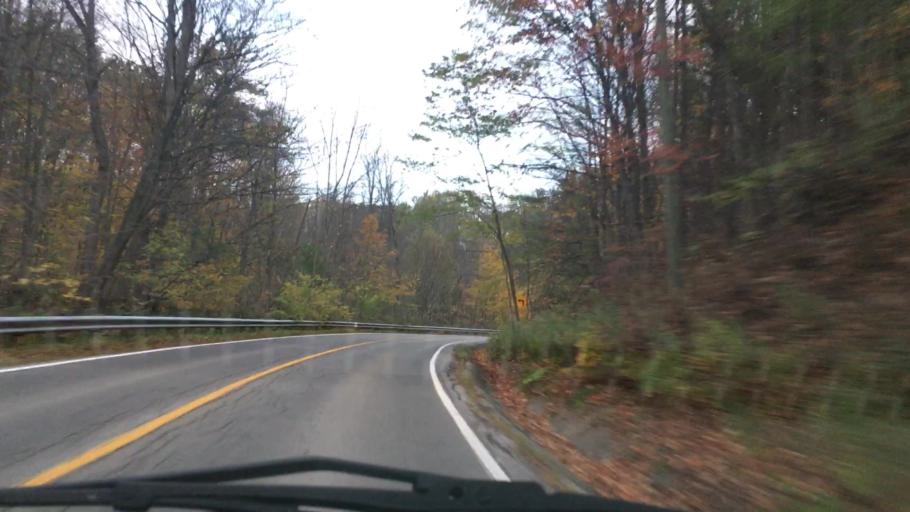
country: CA
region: Ontario
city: Hamilton
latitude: 43.3179
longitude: -79.8923
